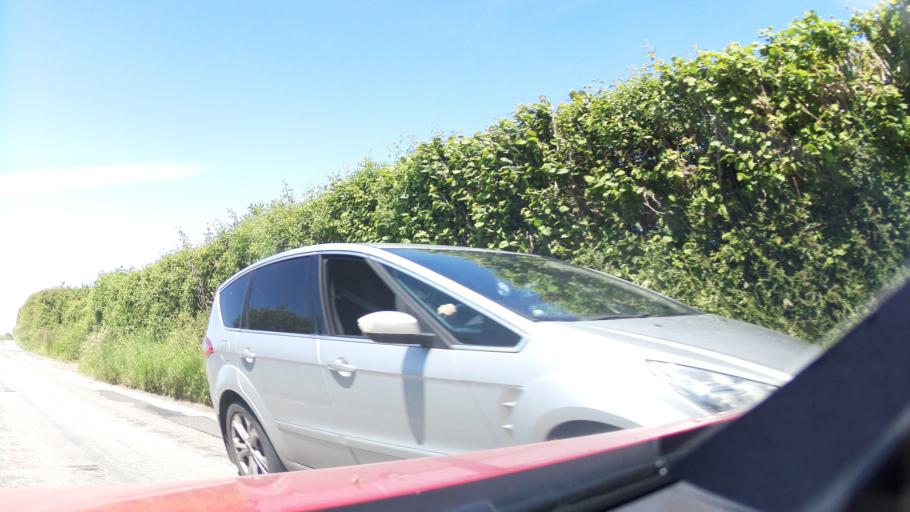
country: GB
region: Wales
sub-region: Monmouthshire
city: Caldicot
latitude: 51.5933
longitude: -2.7297
